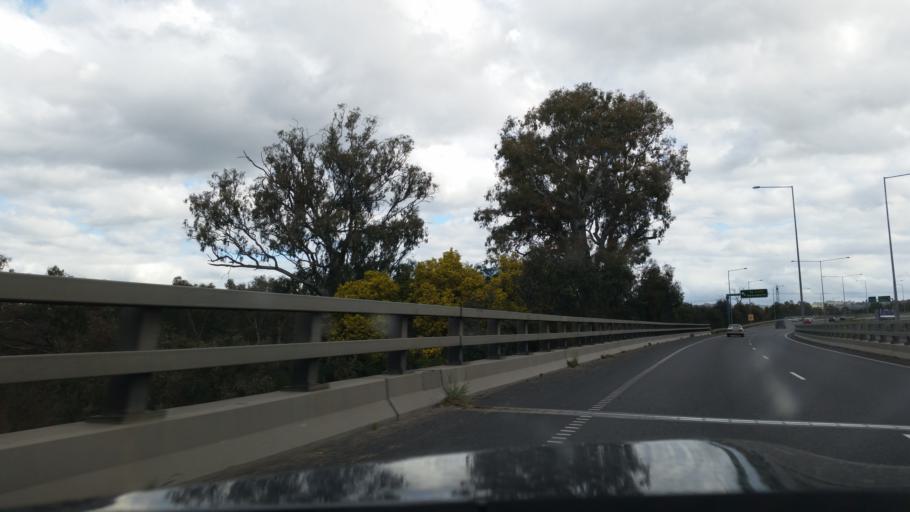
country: AU
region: New South Wales
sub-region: Albury Municipality
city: South Albury
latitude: -36.1064
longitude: 146.9044
